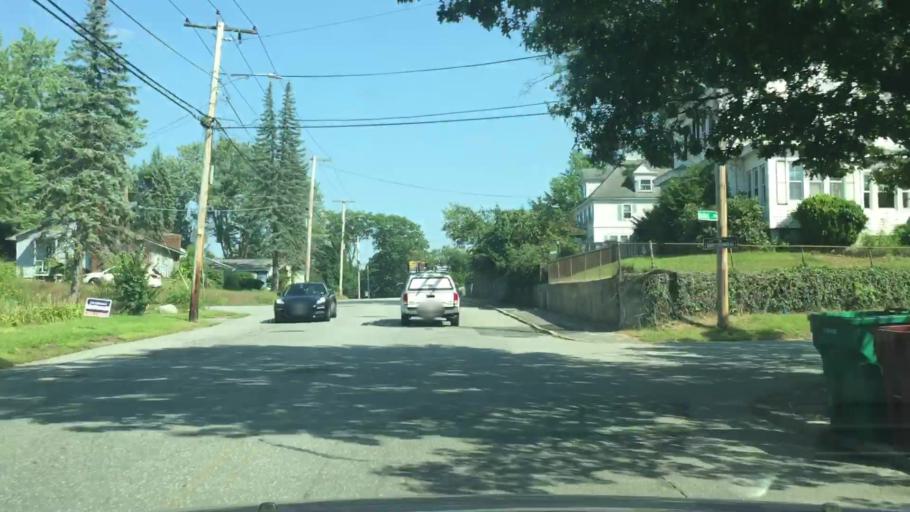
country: US
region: Massachusetts
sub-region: Middlesex County
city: Lowell
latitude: 42.6454
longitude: -71.3534
